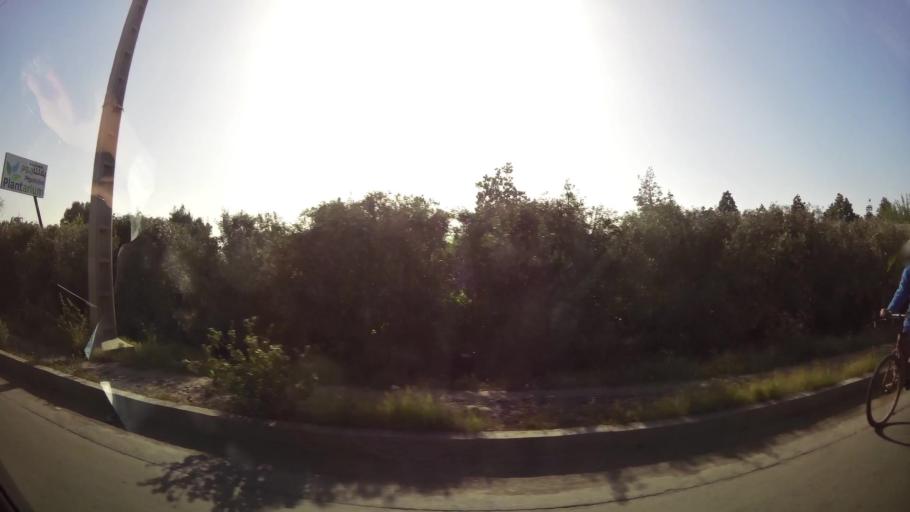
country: MA
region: Souss-Massa-Draa
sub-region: Inezgane-Ait Mellou
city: Inezgane
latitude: 30.3619
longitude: -9.5060
